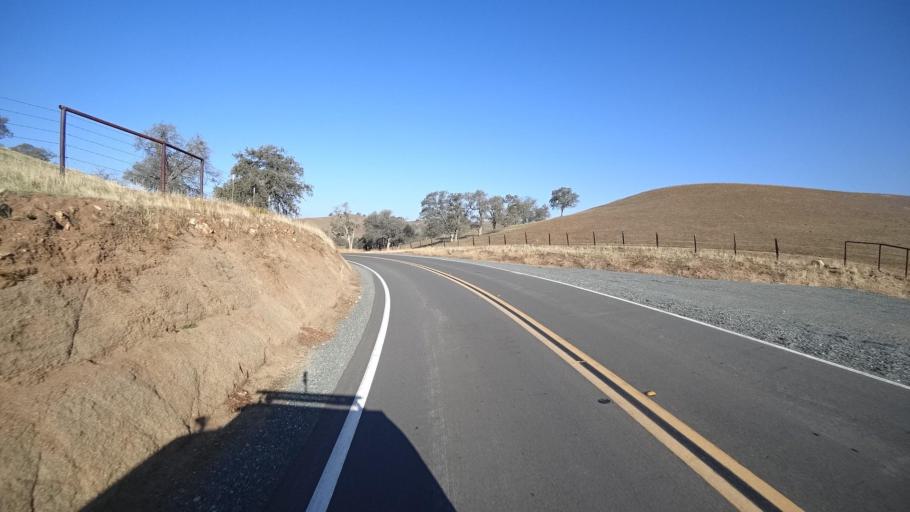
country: US
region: California
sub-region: Tulare County
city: Richgrove
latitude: 35.7132
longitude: -118.8446
